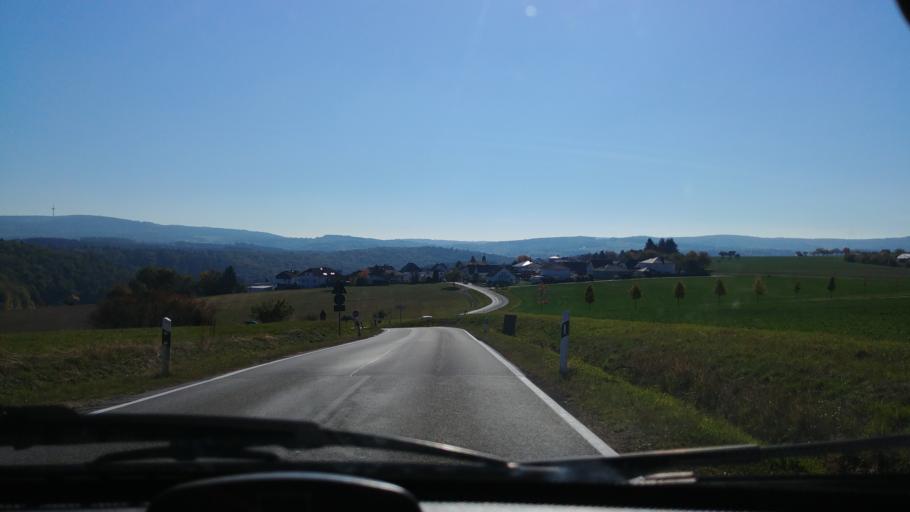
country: DE
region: Hesse
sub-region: Regierungsbezirk Darmstadt
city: Bad Schwalbach
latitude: 50.1652
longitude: 8.1046
